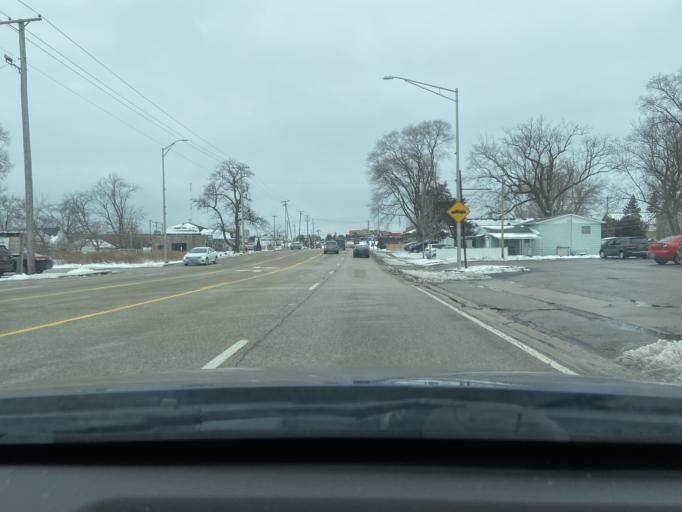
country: US
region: Illinois
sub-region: Lake County
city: Round Lake Beach
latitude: 42.3769
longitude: -88.0897
